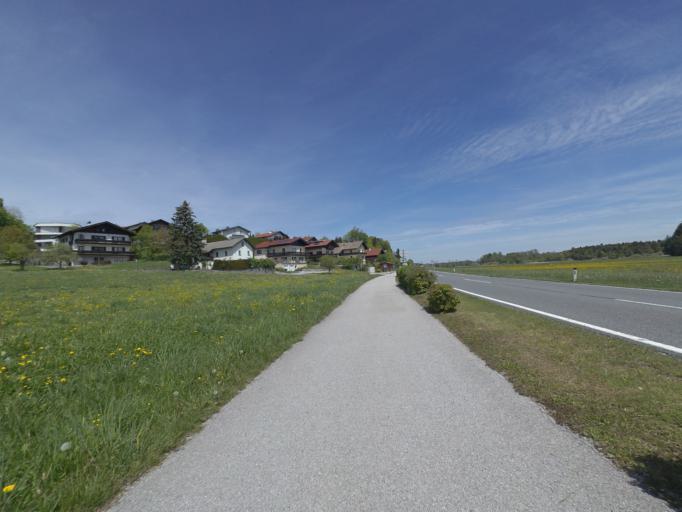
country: AT
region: Salzburg
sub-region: Politischer Bezirk Salzburg-Umgebung
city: Seeham
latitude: 47.9759
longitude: 13.0782
